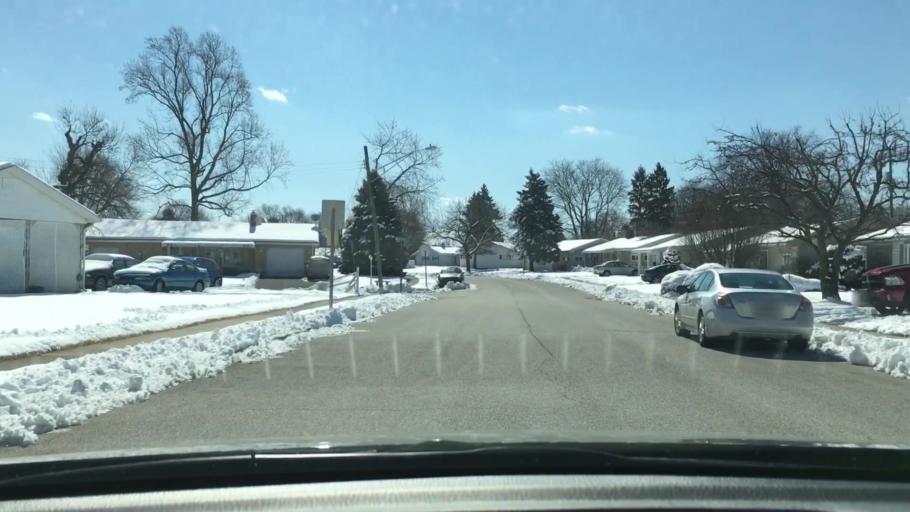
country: US
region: Pennsylvania
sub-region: York County
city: North York
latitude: 39.9780
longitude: -76.7509
